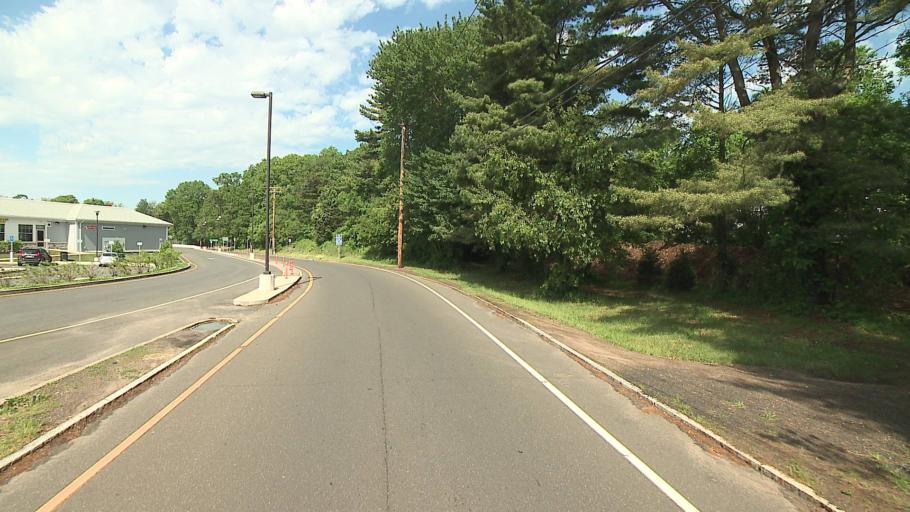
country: US
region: Connecticut
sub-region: Fairfield County
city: Fairfield
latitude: 41.1486
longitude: -73.2559
